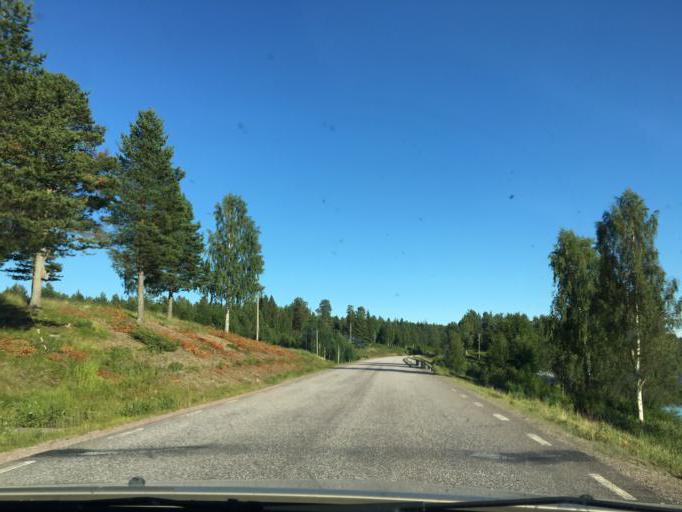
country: SE
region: Norrbotten
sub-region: Kalix Kommun
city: Rolfs
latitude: 65.9168
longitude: 22.9200
